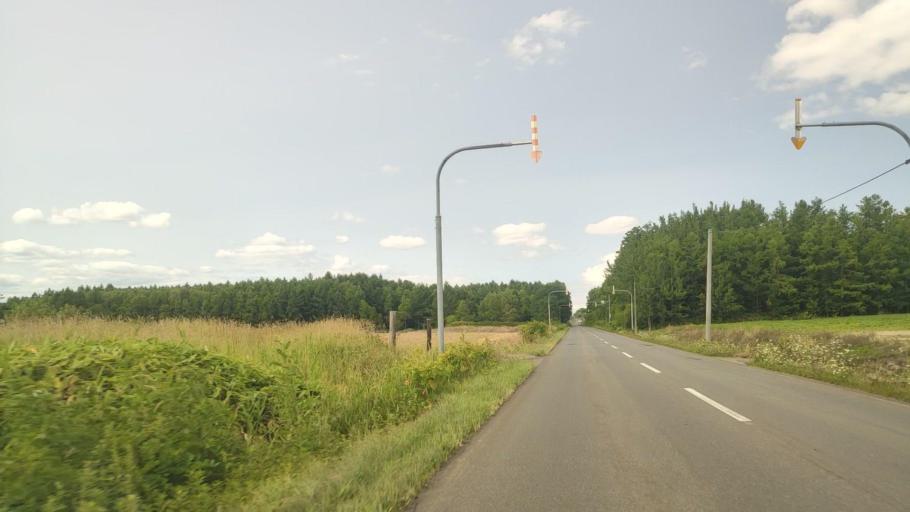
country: JP
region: Hokkaido
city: Nayoro
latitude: 44.2413
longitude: 142.4157
